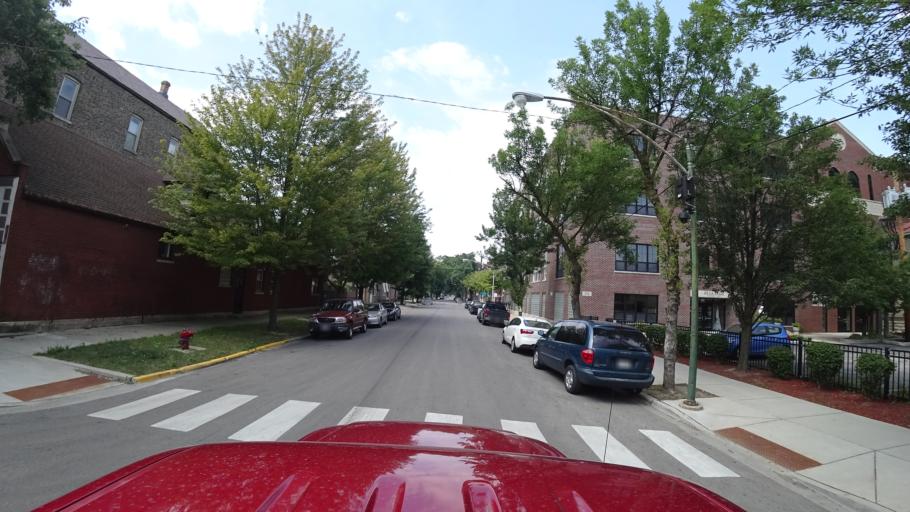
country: US
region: Illinois
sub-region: Cook County
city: Chicago
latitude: 41.8353
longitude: -87.6523
